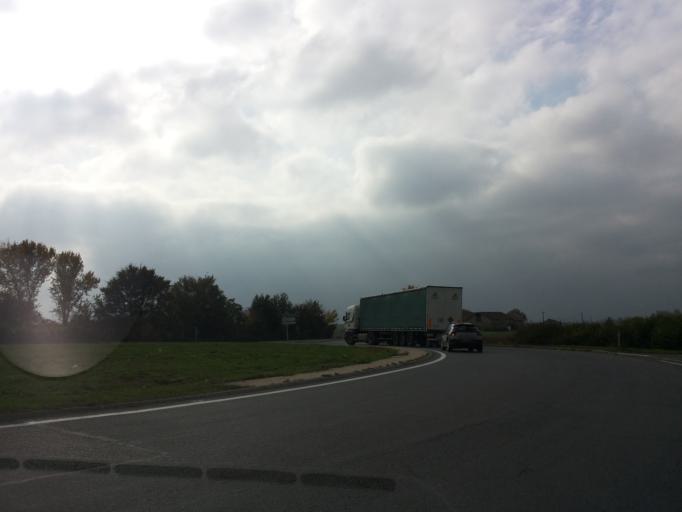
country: FR
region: Lorraine
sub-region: Departement de la Moselle
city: Solgne
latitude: 48.9830
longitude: 6.2876
